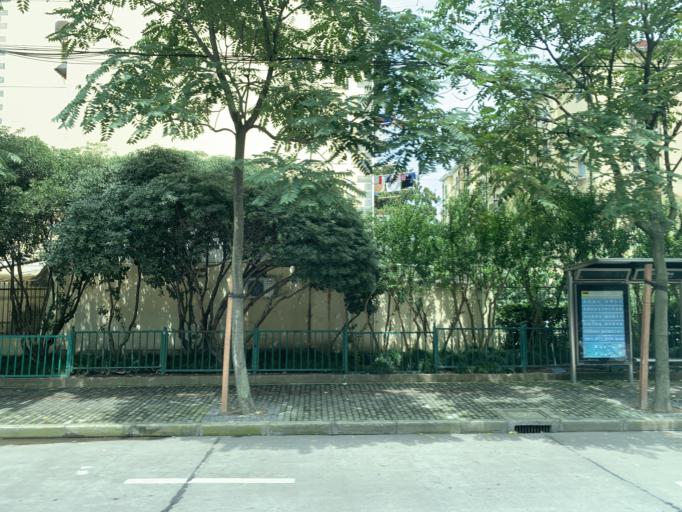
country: CN
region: Shanghai Shi
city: Pudong
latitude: 31.2496
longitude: 121.5749
